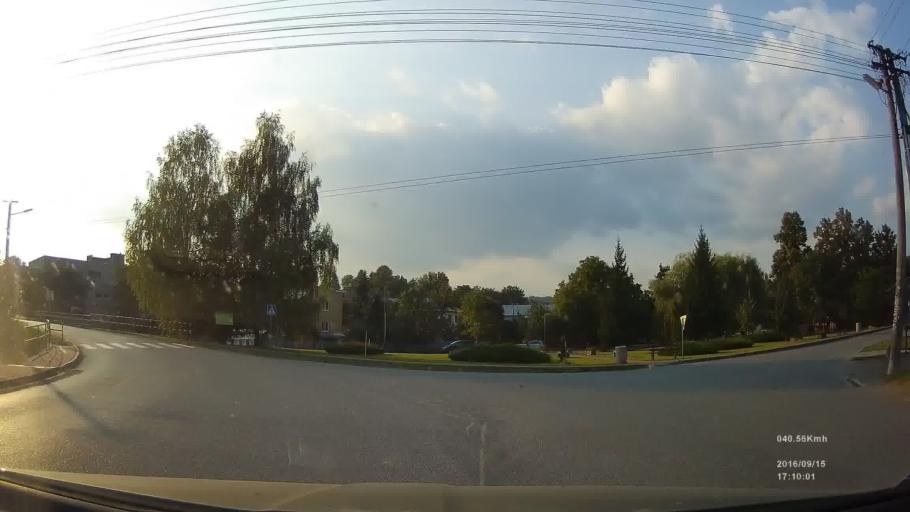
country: SK
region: Presovsky
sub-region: Okres Presov
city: Presov
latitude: 48.9179
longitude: 21.1187
